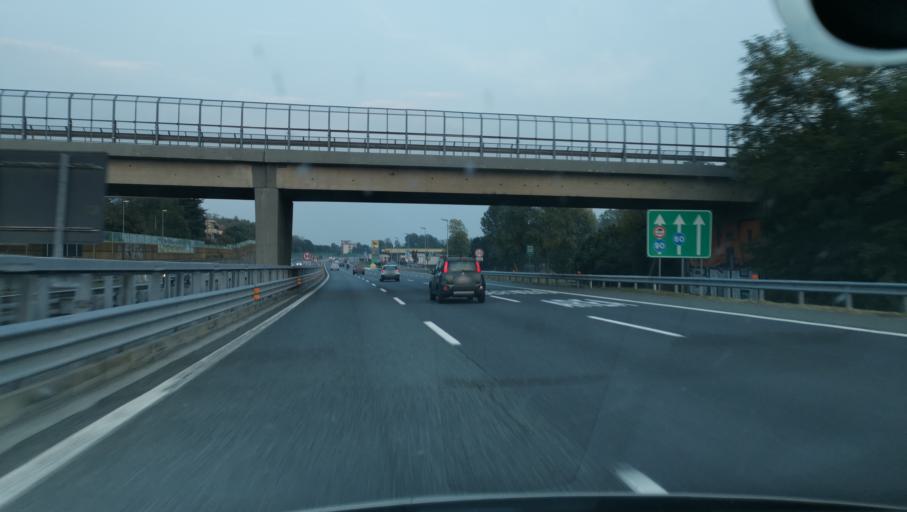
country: IT
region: Piedmont
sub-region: Provincia di Torino
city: Alpignano
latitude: 45.0830
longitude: 7.5112
